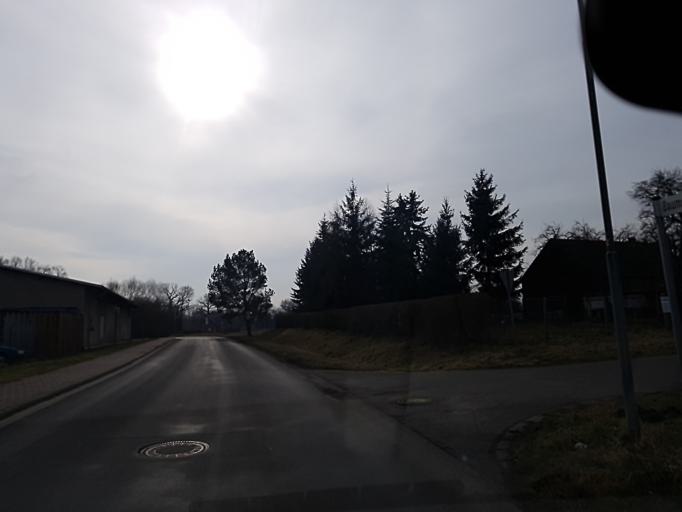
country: DE
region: Brandenburg
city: Doberlug-Kirchhain
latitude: 51.6239
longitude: 13.5567
